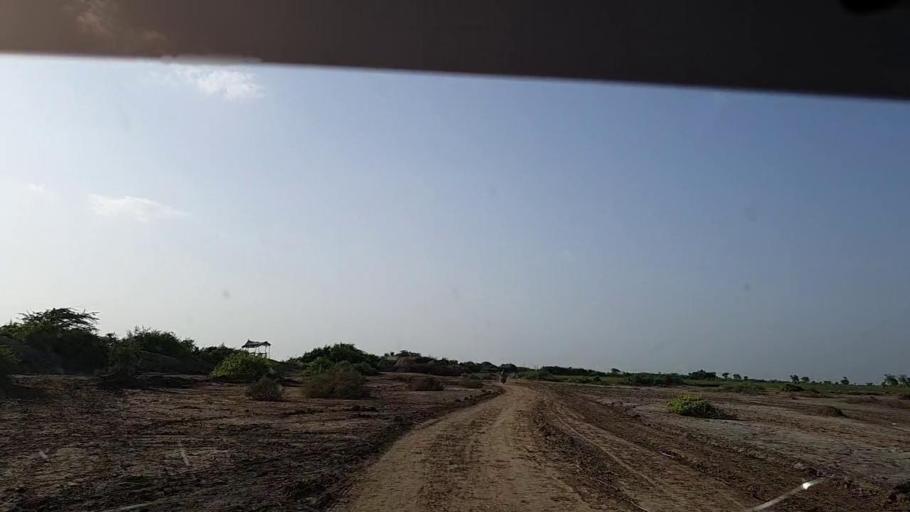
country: PK
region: Sindh
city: Badin
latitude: 24.5718
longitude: 68.8770
